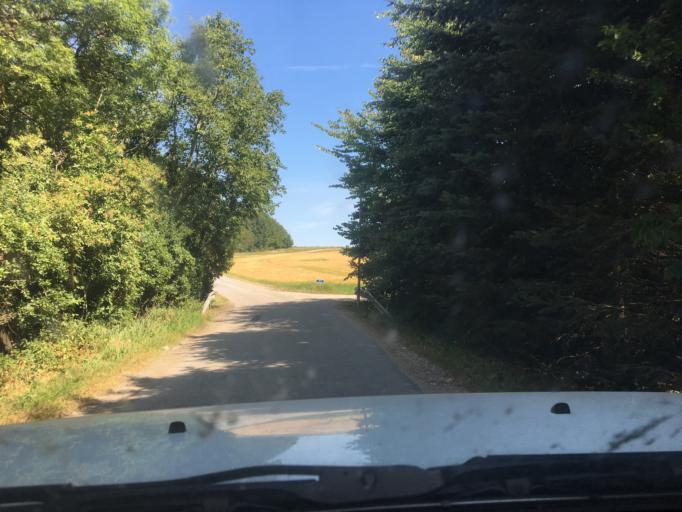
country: DK
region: Central Jutland
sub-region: Favrskov Kommune
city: Hadsten
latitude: 56.3930
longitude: 10.0660
